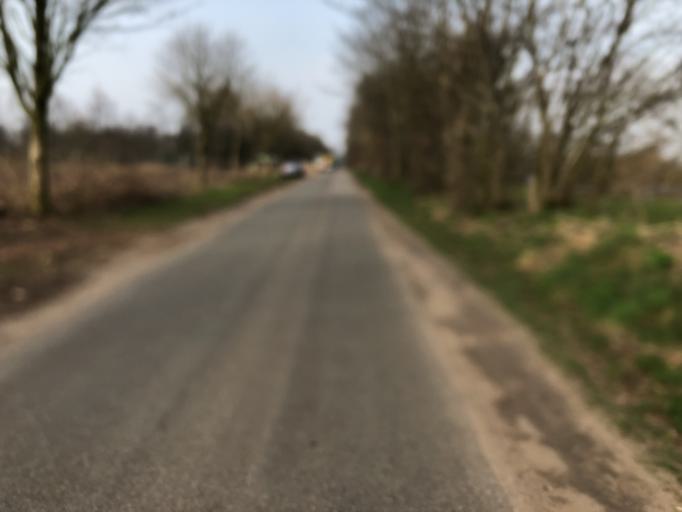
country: DE
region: Schleswig-Holstein
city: Wanderup
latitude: 54.7023
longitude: 9.3561
